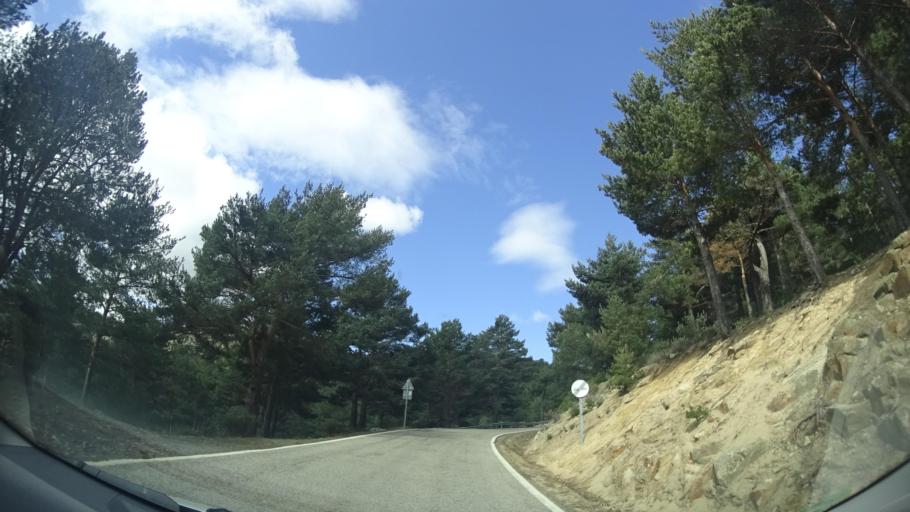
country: ES
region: Madrid
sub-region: Provincia de Madrid
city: Canencia
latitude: 40.8664
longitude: -3.7602
